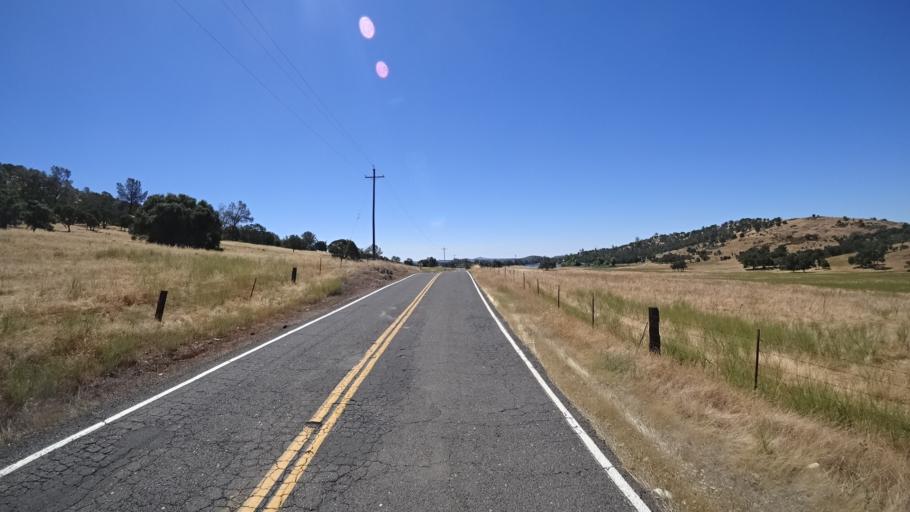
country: US
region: California
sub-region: Calaveras County
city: Copperopolis
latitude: 37.9936
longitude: -120.6527
